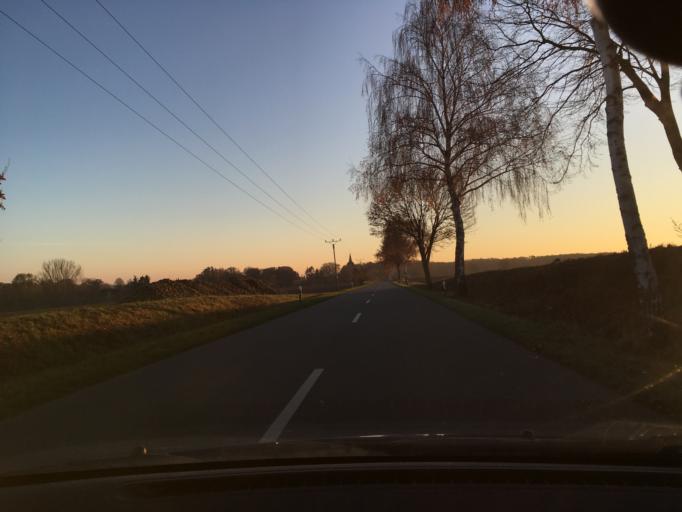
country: DE
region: Lower Saxony
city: Natendorf
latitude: 53.0863
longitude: 10.4672
